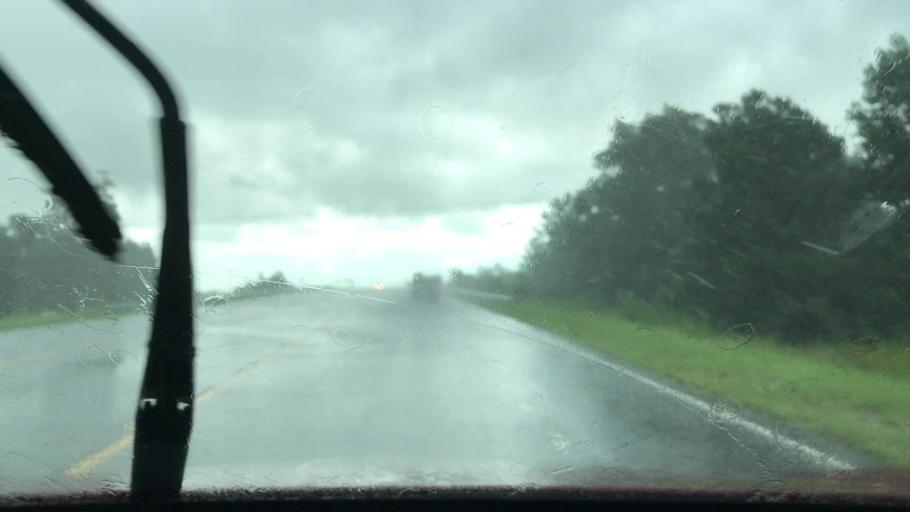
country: US
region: South Carolina
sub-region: Horry County
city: Loris
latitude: 33.9029
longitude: -78.8637
